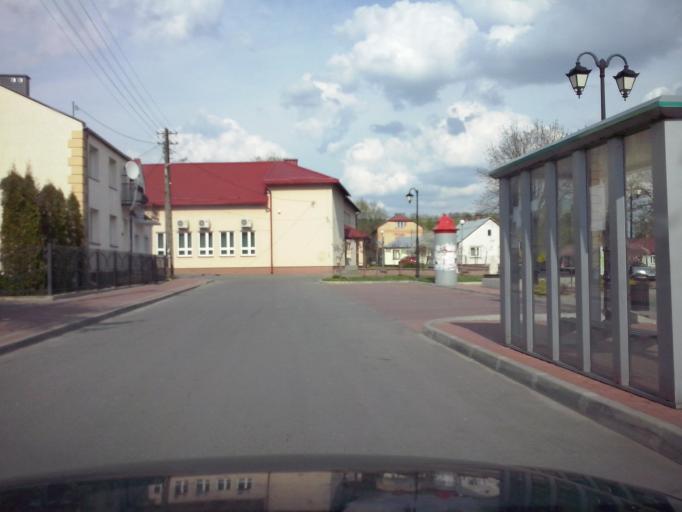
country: PL
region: Subcarpathian Voivodeship
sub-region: Powiat nizanski
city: Krzeszow
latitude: 50.4035
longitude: 22.3404
